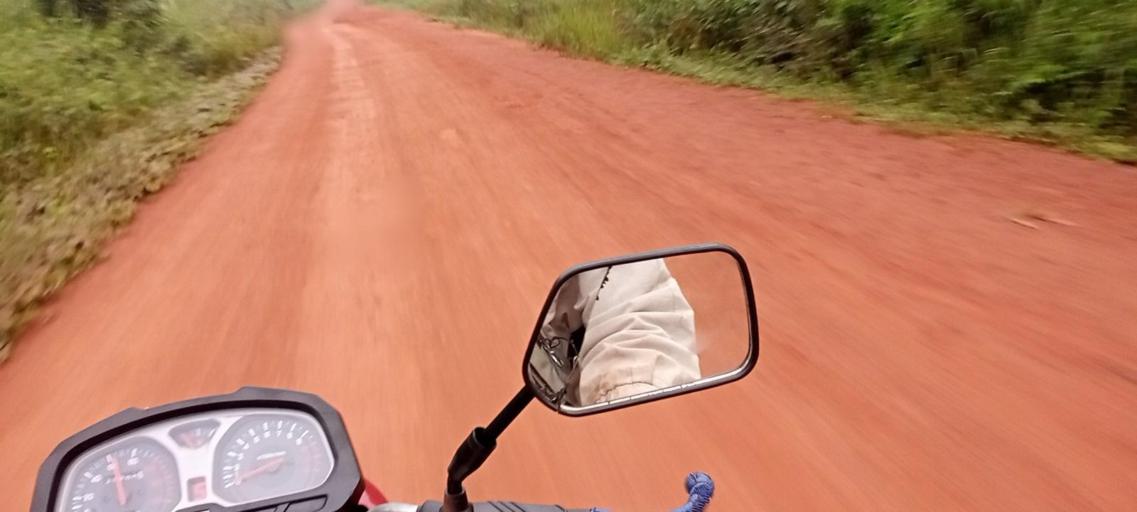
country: CD
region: Eastern Province
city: Kisangani
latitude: -0.0839
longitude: 25.6066
